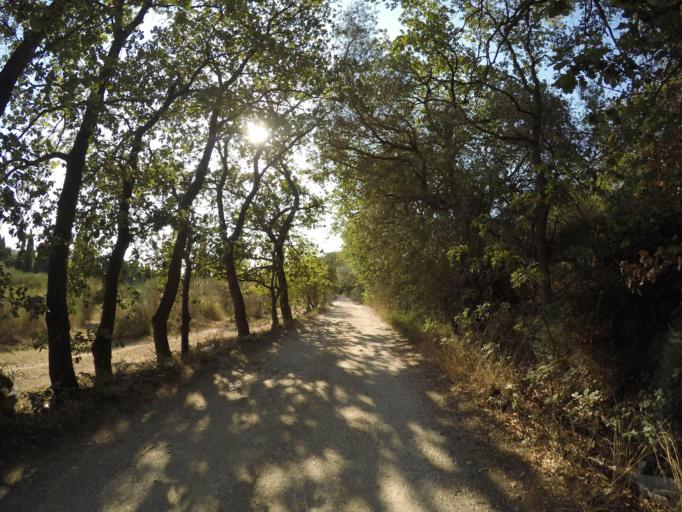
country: FR
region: Languedoc-Roussillon
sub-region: Departement des Pyrenees-Orientales
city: Pollestres
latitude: 42.6670
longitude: 2.8714
